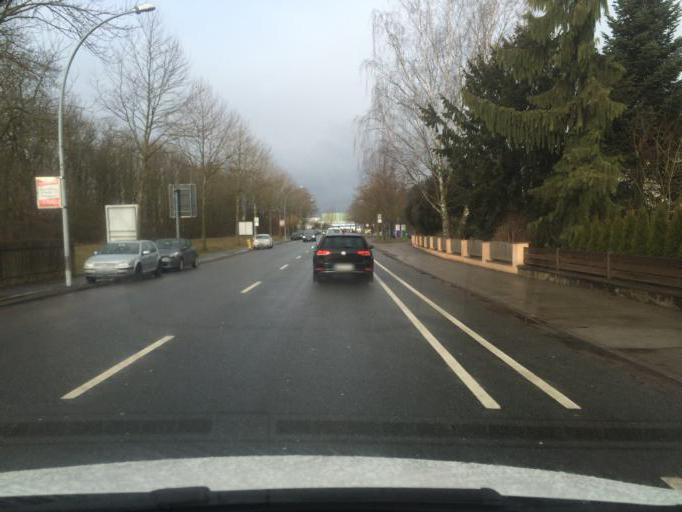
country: DE
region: Lower Saxony
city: Duderstadt
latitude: 51.5160
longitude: 10.2485
